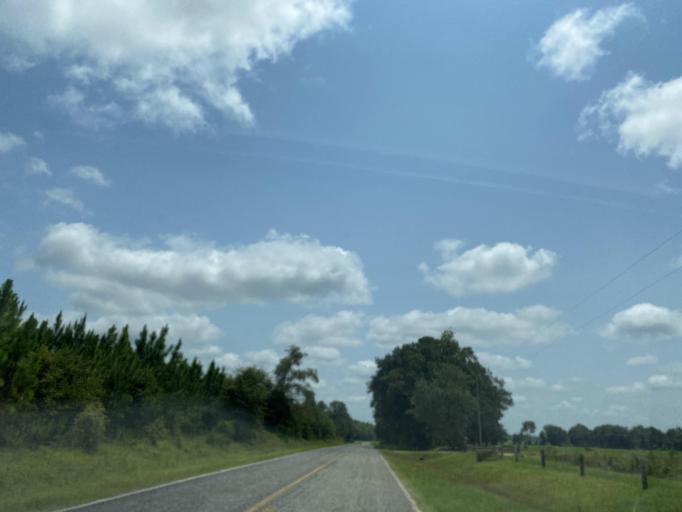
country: US
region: Georgia
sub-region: Telfair County
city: Lumber City
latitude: 32.0099
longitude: -82.7232
